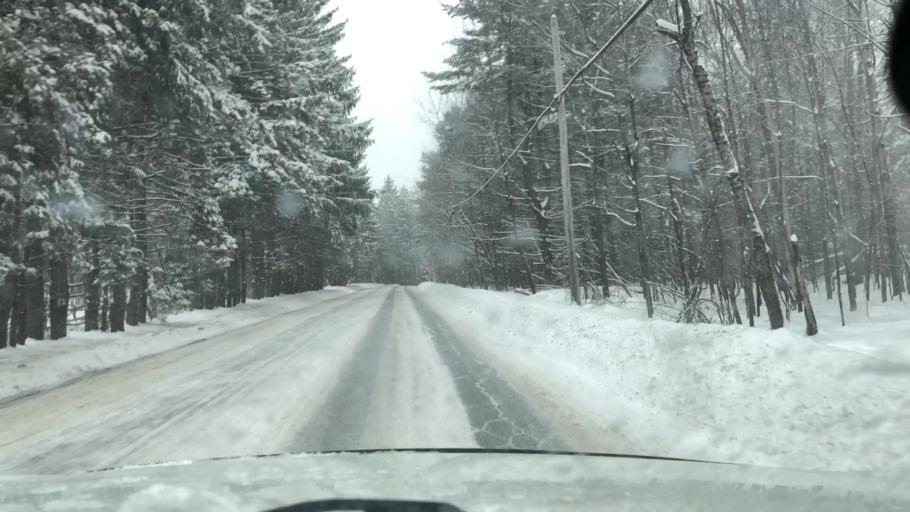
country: CA
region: Quebec
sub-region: Outaouais
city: Gatineau
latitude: 45.5136
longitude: -75.8380
